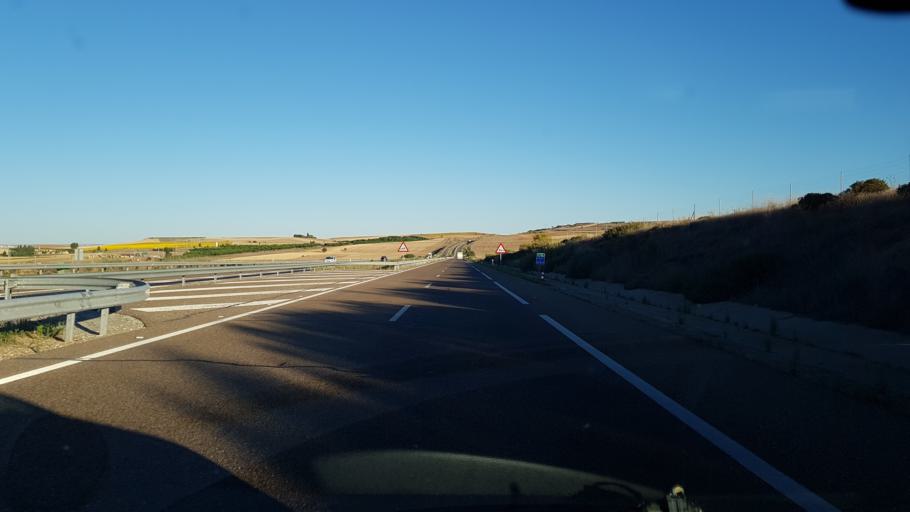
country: ES
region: Castille and Leon
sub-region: Provincia de Zamora
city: Fresno de la Ribera
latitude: 41.5425
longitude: -5.5612
